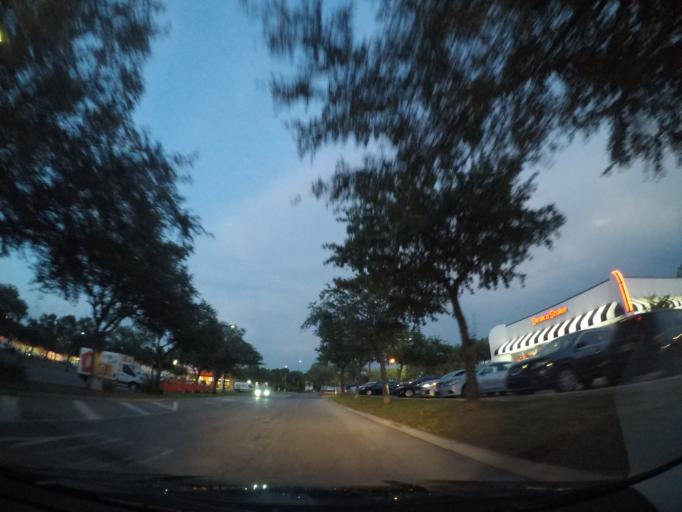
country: US
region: Florida
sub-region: Sarasota County
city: Lake Sarasota
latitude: 27.2931
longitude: -82.4516
